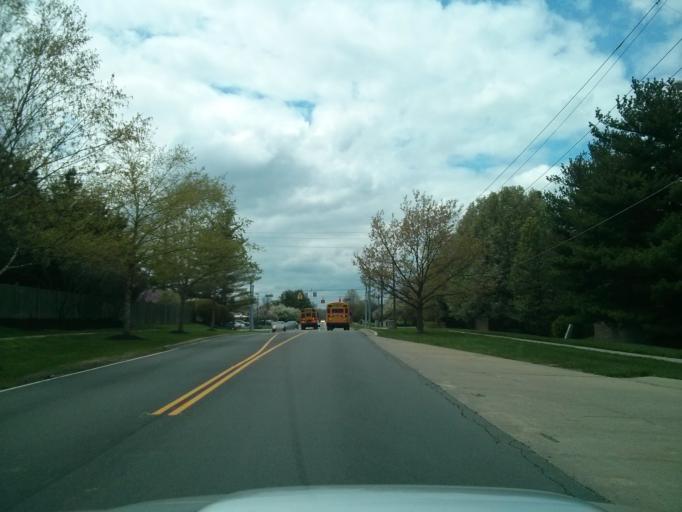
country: US
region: Indiana
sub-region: Hamilton County
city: Carmel
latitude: 39.9712
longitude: -86.0881
